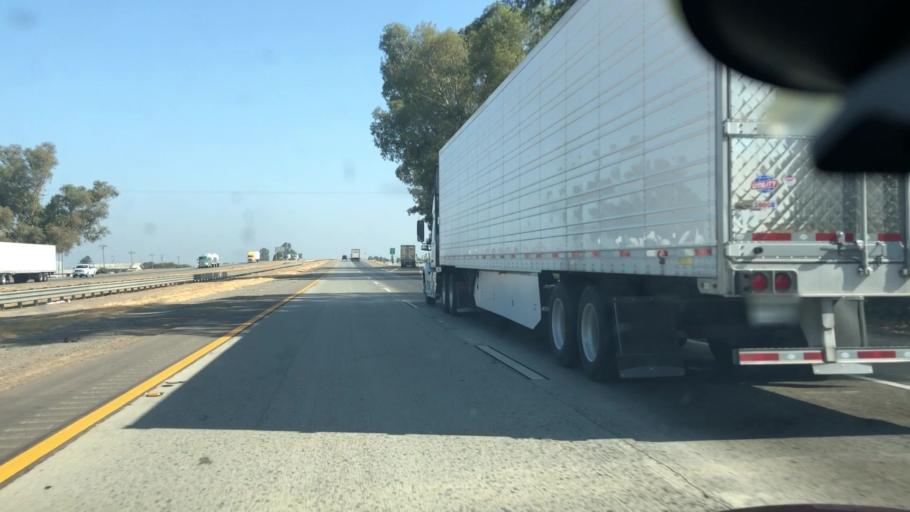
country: US
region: California
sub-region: San Joaquin County
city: Thornton
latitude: 38.1413
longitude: -121.3991
